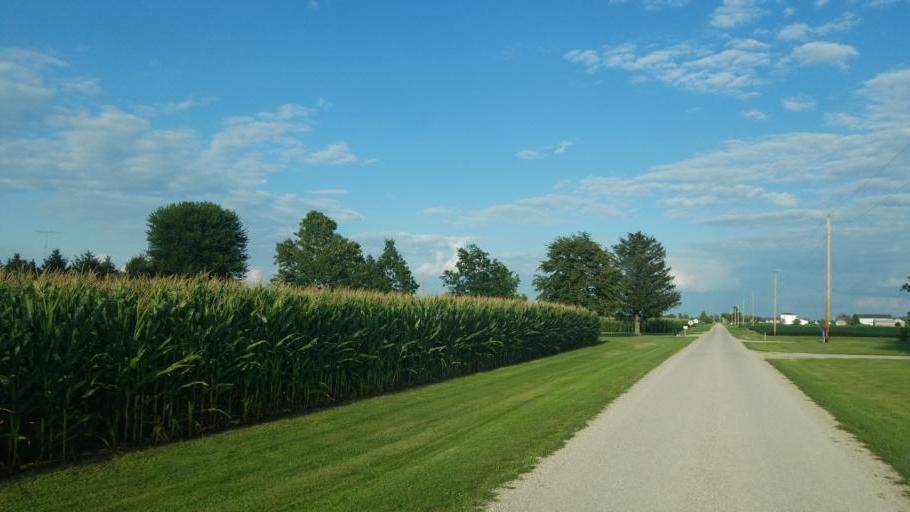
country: US
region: Ohio
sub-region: Sandusky County
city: Mount Carmel
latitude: 41.1103
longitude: -82.9562
